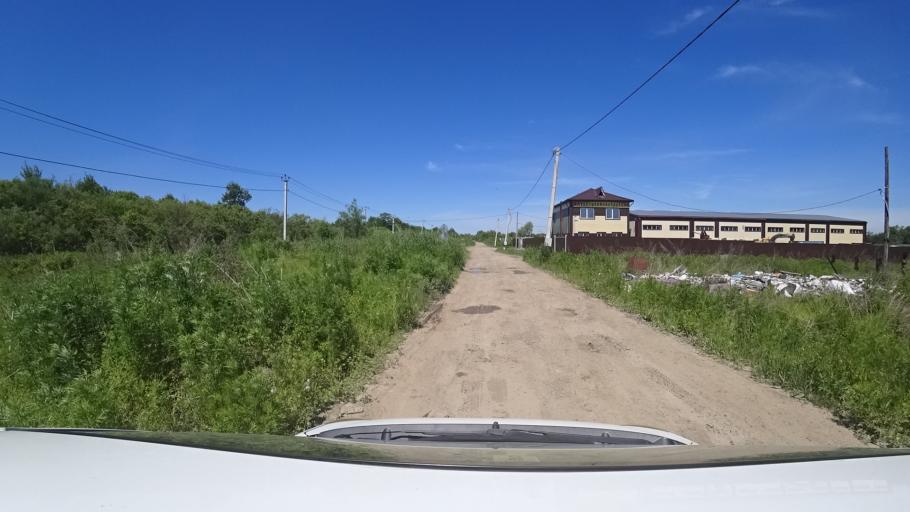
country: RU
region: Khabarovsk Krai
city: Topolevo
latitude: 48.4833
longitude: 135.1752
